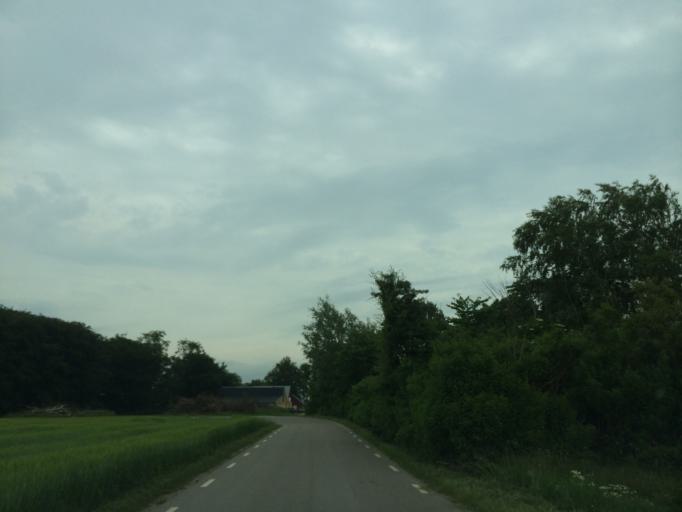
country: SE
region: Skane
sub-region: Kavlinge Kommun
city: Loddekopinge
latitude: 55.7525
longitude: 13.0665
